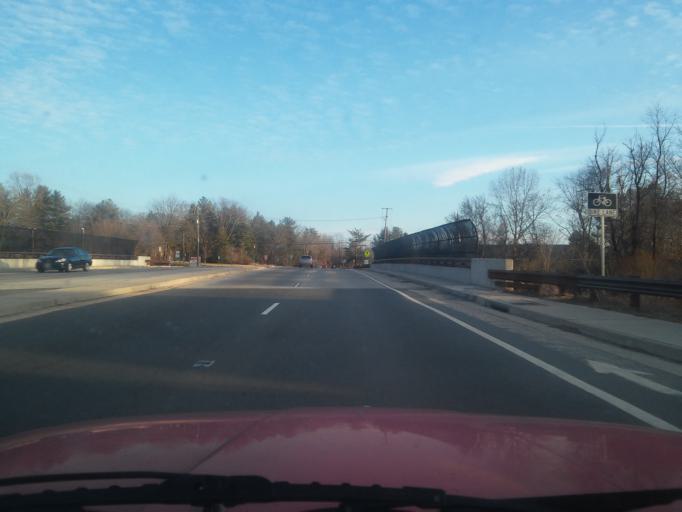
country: US
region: Virginia
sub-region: City of Charlottesville
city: Charlottesville
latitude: 38.0650
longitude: -78.4649
